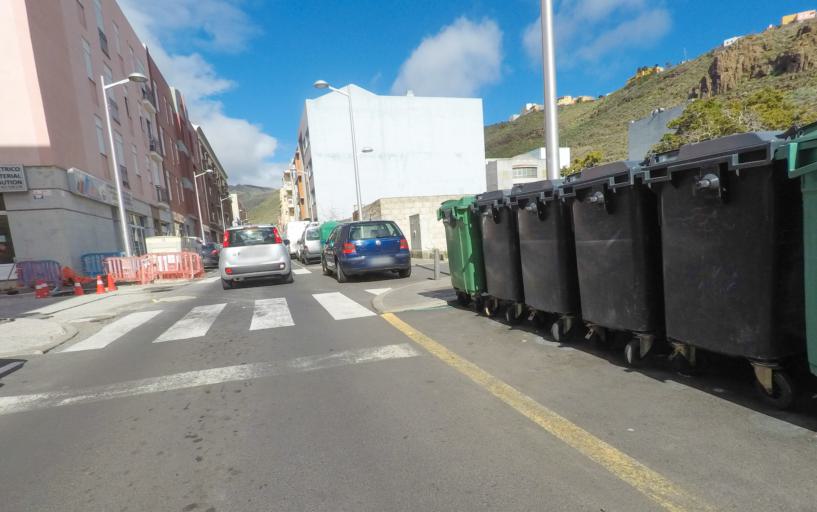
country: ES
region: Canary Islands
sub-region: Provincia de Santa Cruz de Tenerife
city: San Sebastian de la Gomera
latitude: 28.0930
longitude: -17.1136
